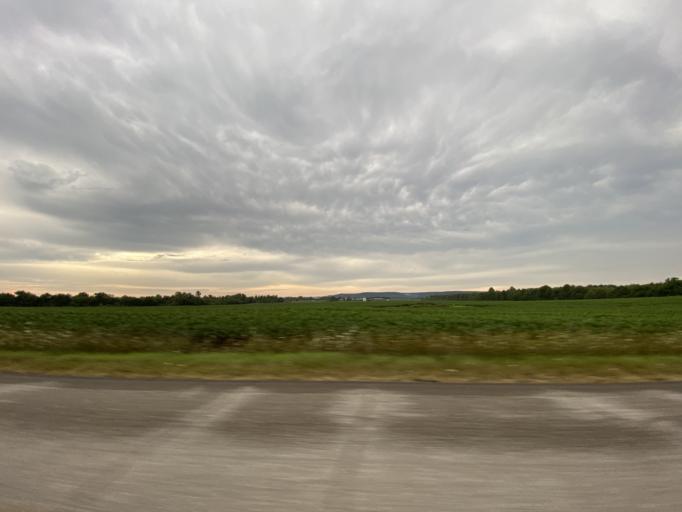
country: US
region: Alabama
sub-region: Lawrence County
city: Moulton
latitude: 34.4640
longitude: -87.4979
